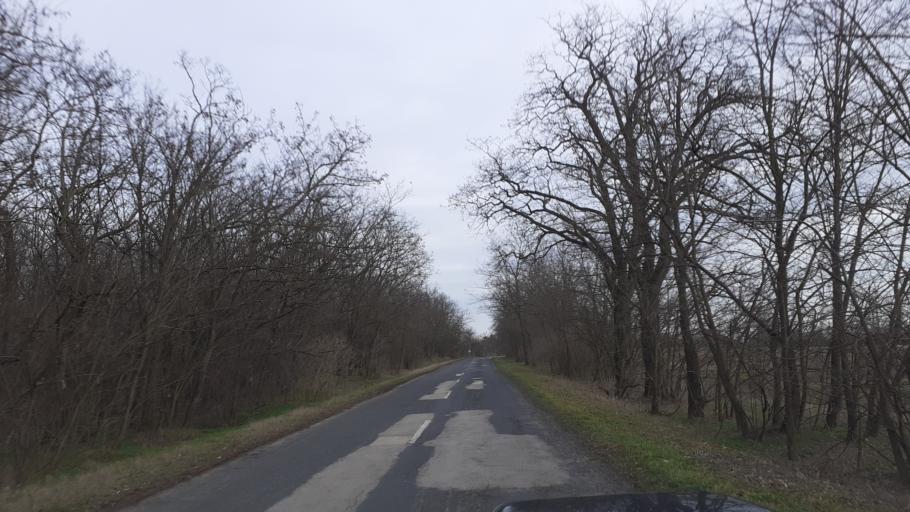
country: HU
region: Fejer
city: Szabadbattyan
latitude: 47.1230
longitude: 18.3942
